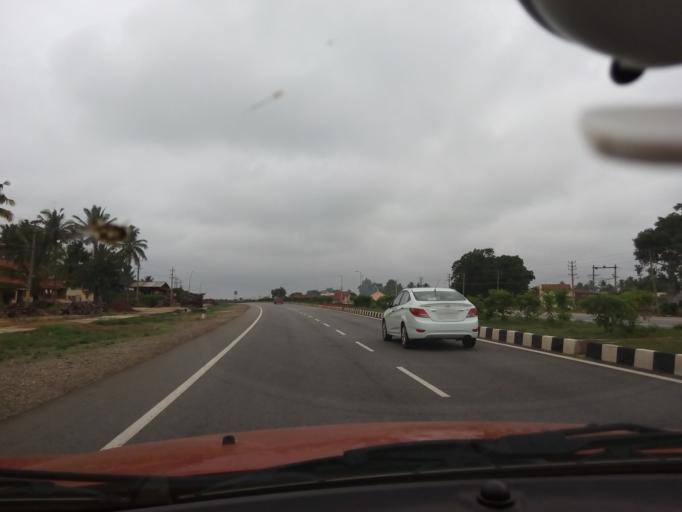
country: IN
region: Karnataka
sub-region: Hassan
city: Shravanabelagola
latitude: 12.9489
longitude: 76.5561
